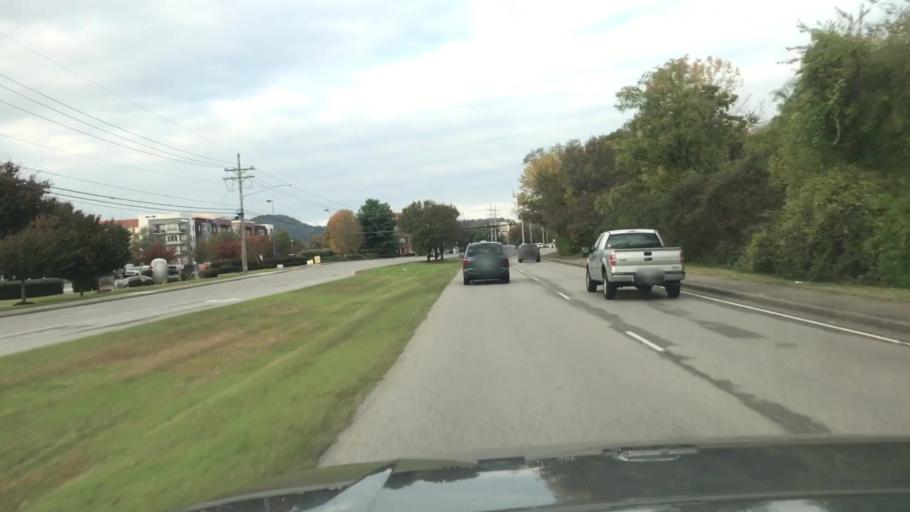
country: US
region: Tennessee
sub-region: Williamson County
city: Franklin
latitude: 35.9538
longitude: -86.8176
